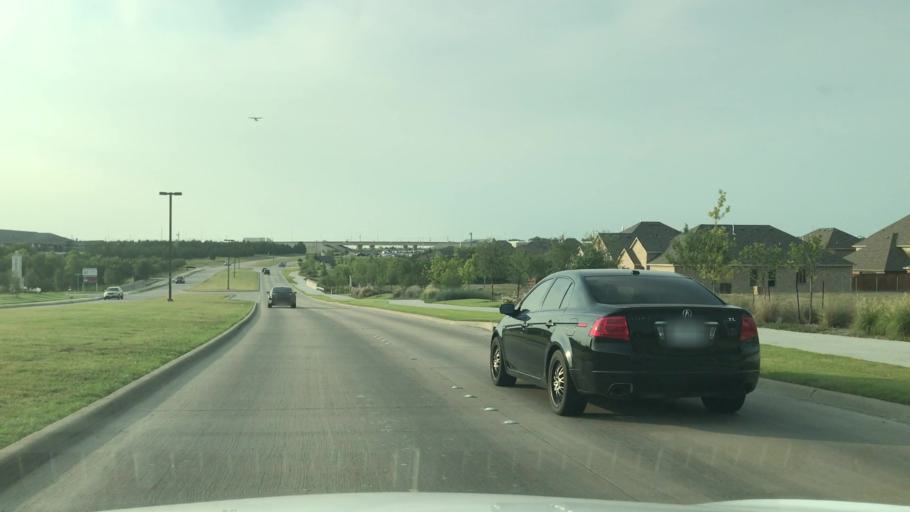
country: US
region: Texas
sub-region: Rockwall County
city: Rockwall
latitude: 32.9097
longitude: -96.4313
